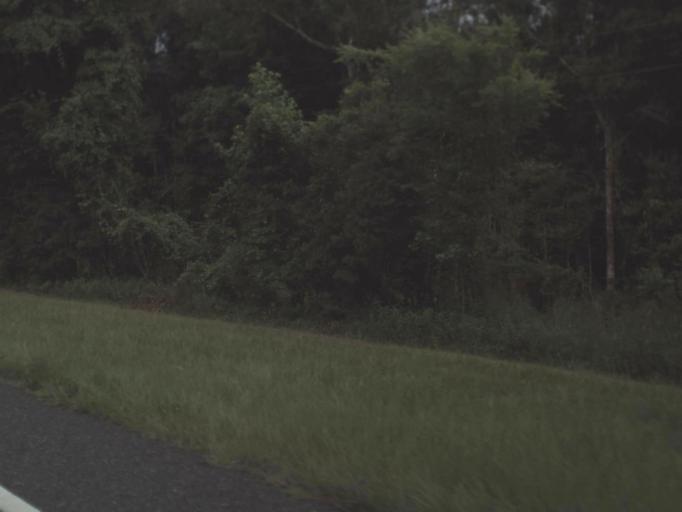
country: US
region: Florida
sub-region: Levy County
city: Inglis
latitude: 29.1810
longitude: -82.6723
